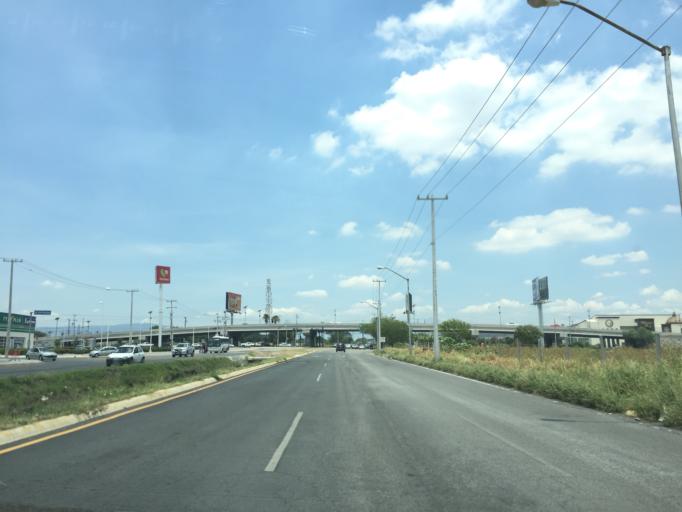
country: MX
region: Nuevo Leon
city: Apodaca
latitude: 25.7661
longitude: -100.1892
